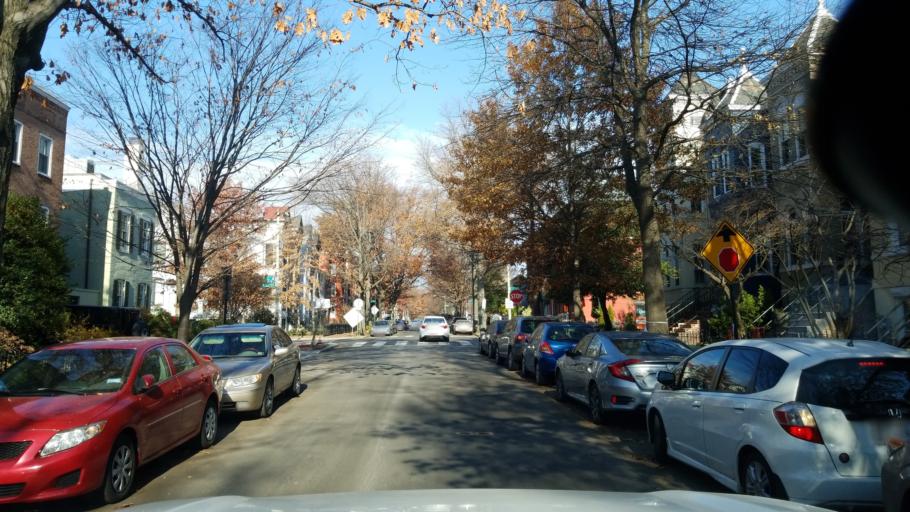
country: US
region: Washington, D.C.
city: Washington, D.C.
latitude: 38.8856
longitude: -77.0020
